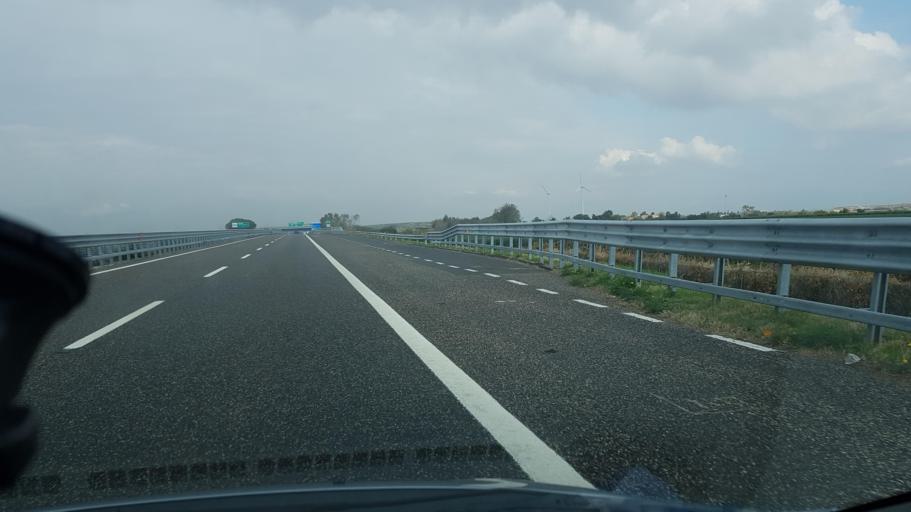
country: IT
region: Apulia
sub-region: Provincia di Foggia
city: Carapelle
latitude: 41.4199
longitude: 15.6635
